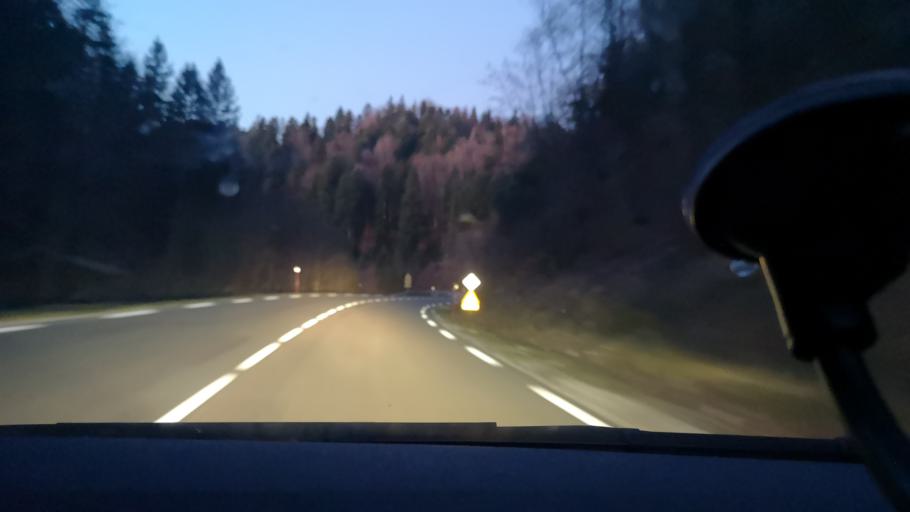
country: FR
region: Franche-Comte
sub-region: Departement du Jura
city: Champagnole
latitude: 46.7555
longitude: 5.9670
